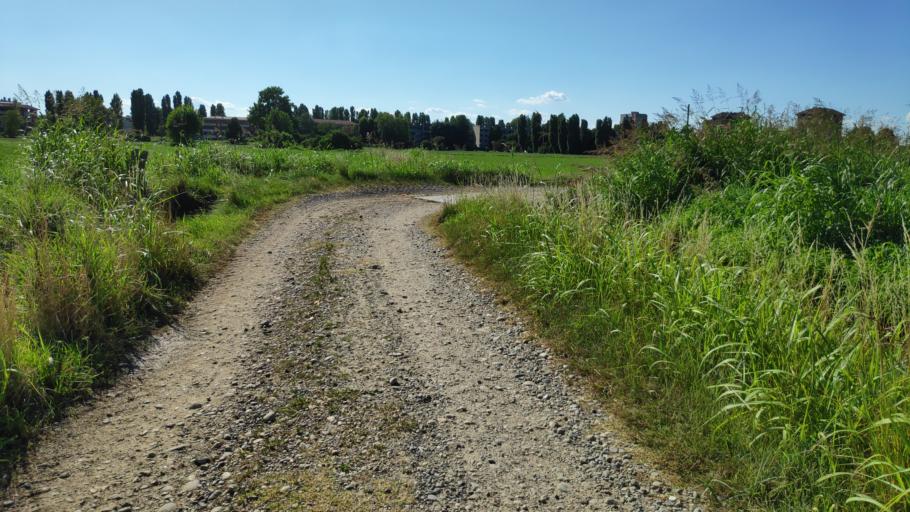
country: IT
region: Lombardy
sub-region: Citta metropolitana di Milano
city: Melzo
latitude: 45.4986
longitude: 9.4380
